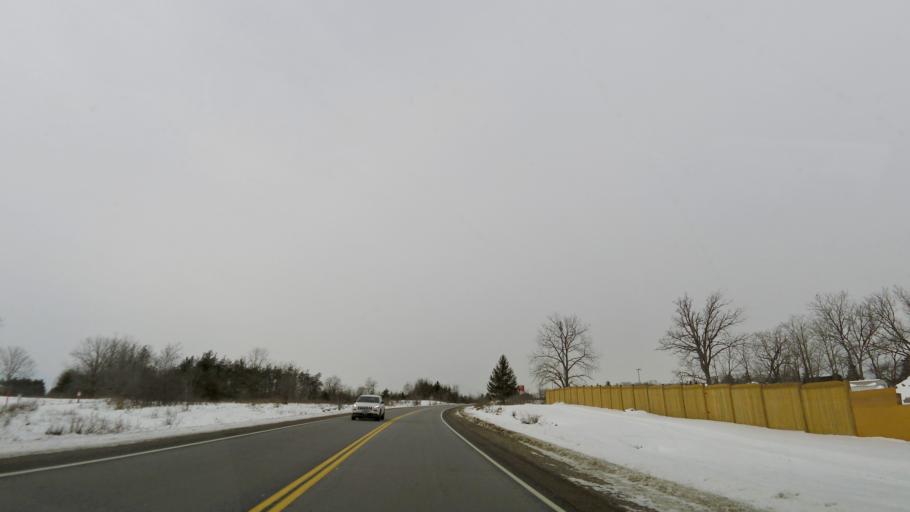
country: CA
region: Ontario
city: Ancaster
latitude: 43.2989
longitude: -80.1277
